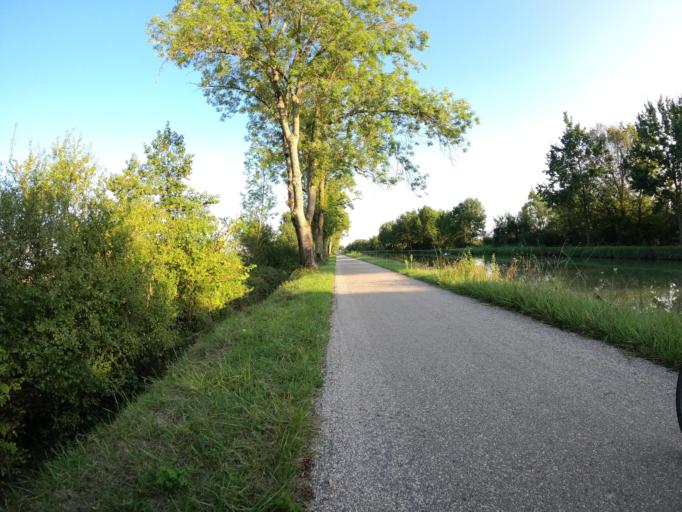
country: FR
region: Midi-Pyrenees
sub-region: Departement du Tarn-et-Garonne
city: Saint-Porquier
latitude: 44.0224
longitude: 1.1645
